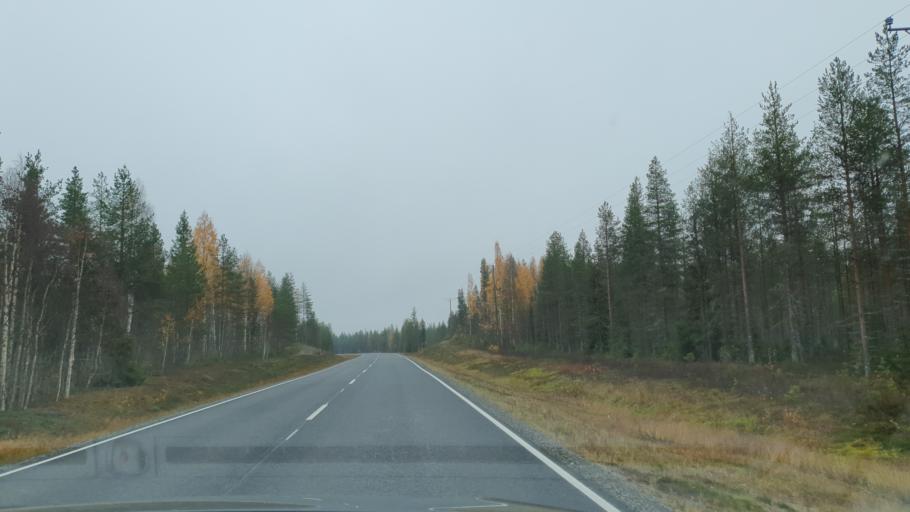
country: FI
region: Lapland
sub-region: Rovaniemi
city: Ranua
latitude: 66.1363
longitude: 26.2755
